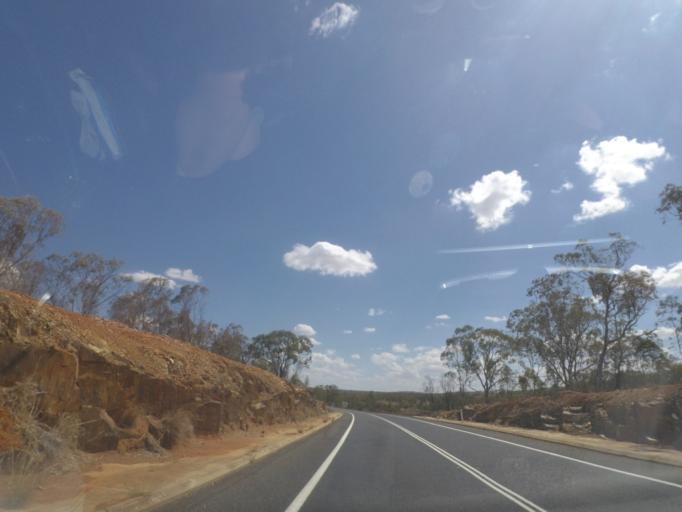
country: AU
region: Queensland
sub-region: Southern Downs
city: Warwick
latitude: -28.2212
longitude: 151.5545
